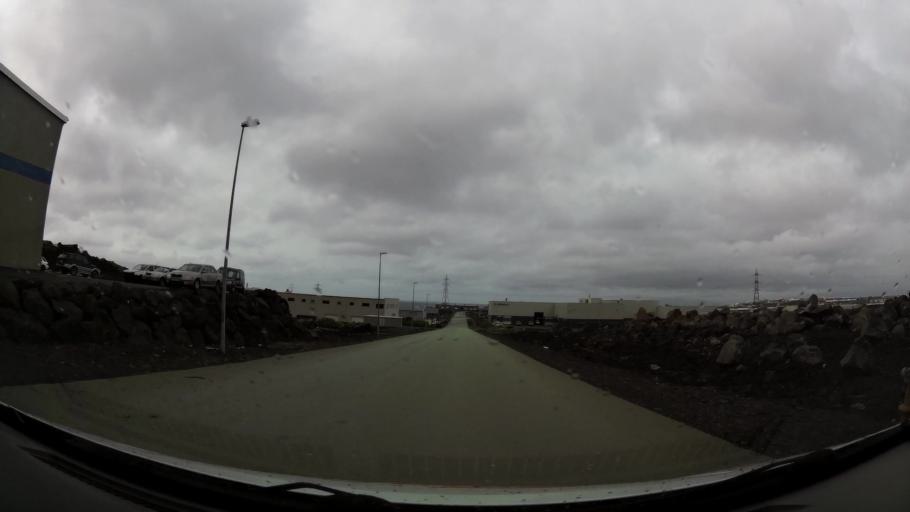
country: IS
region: Capital Region
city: Alftanes
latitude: 64.0391
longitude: -22.0010
